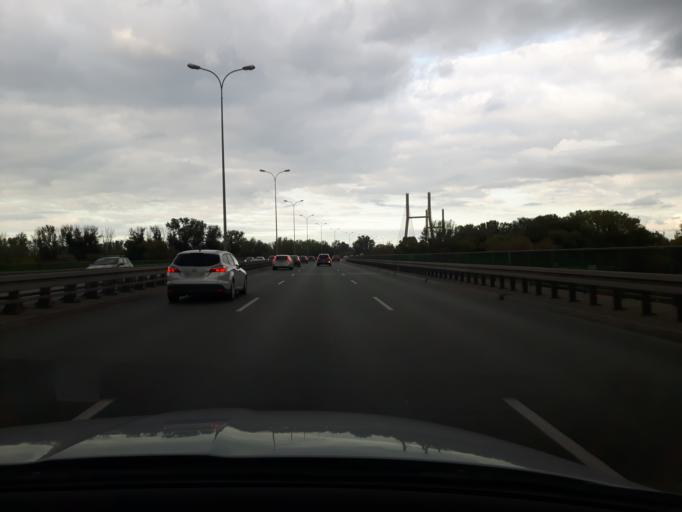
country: PL
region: Masovian Voivodeship
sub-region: Warszawa
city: Praga Poludnie
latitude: 52.2091
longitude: 21.0859
